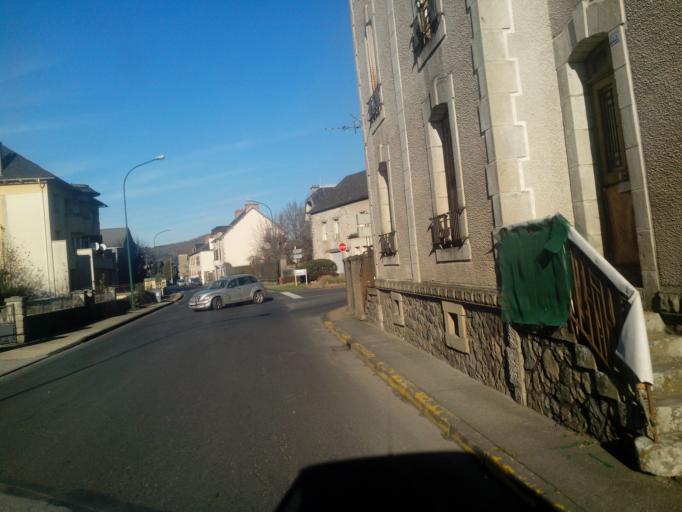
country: FR
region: Limousin
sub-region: Departement de la Correze
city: Bort-les-Orgues
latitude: 45.3944
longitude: 2.4969
